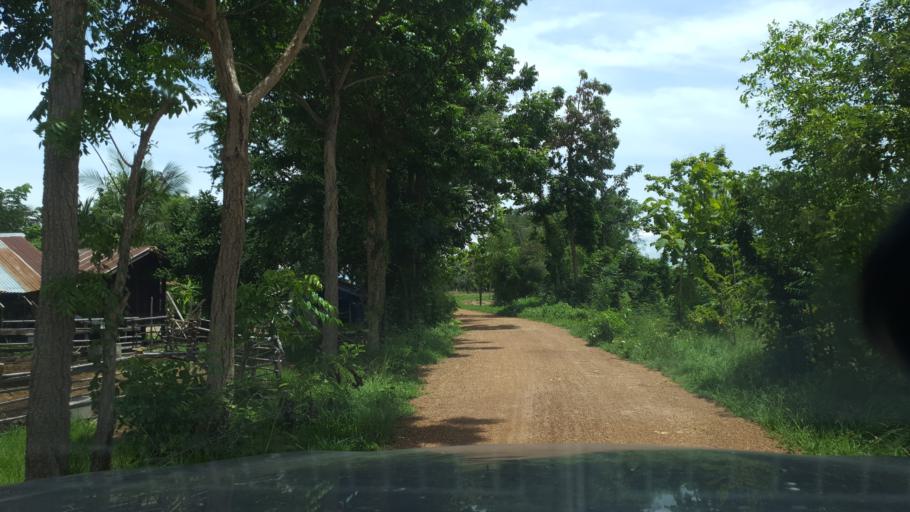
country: TH
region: Sukhothai
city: Ban Na
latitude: 17.0741
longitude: 99.6972
